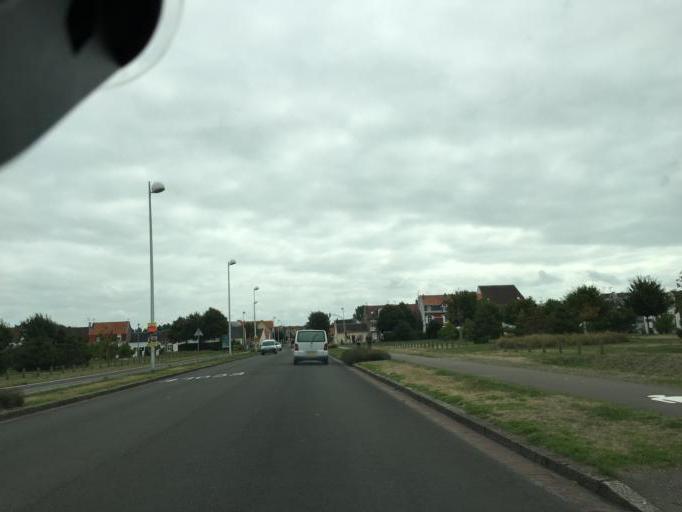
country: FR
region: Nord-Pas-de-Calais
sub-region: Departement du Pas-de-Calais
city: Berck-Plage
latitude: 50.4083
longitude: 1.5781
